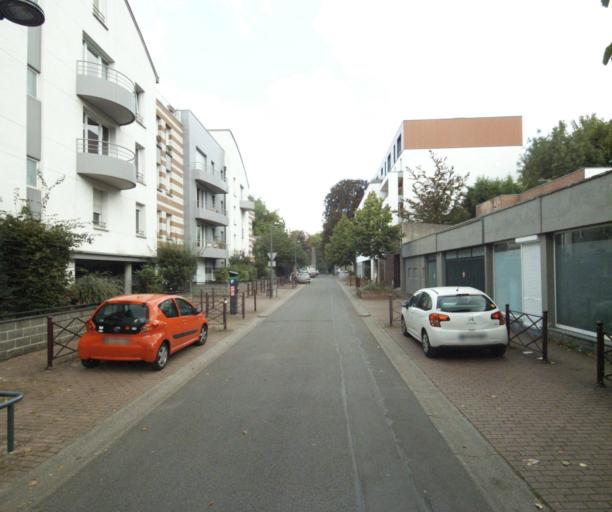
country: FR
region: Nord-Pas-de-Calais
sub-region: Departement du Nord
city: La Madeleine
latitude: 50.6412
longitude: 3.0820
